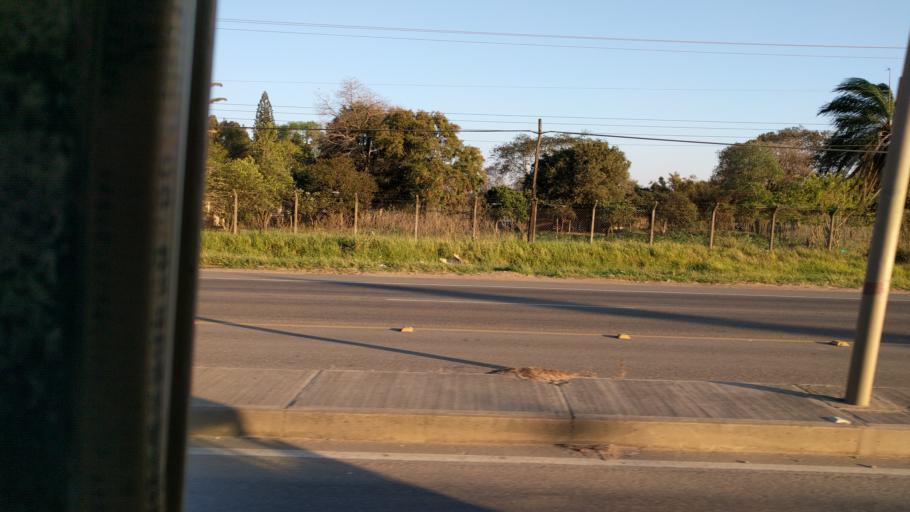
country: BO
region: Santa Cruz
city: Cotoca
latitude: -17.7627
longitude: -63.0275
